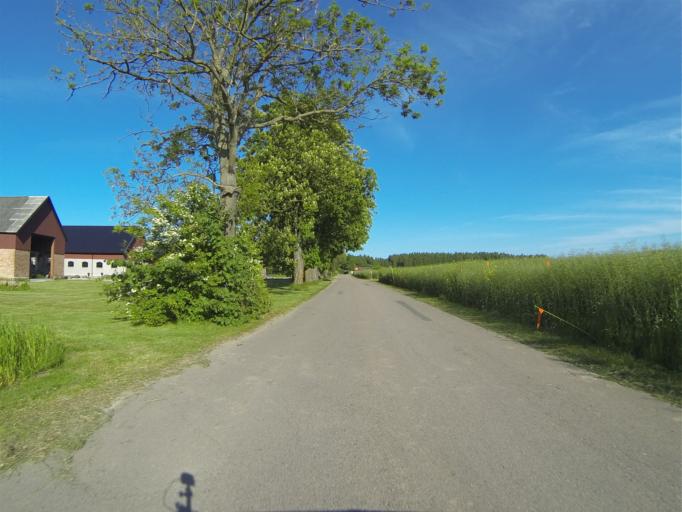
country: SE
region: Skane
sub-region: Lunds Kommun
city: Genarp
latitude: 55.7187
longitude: 13.3804
